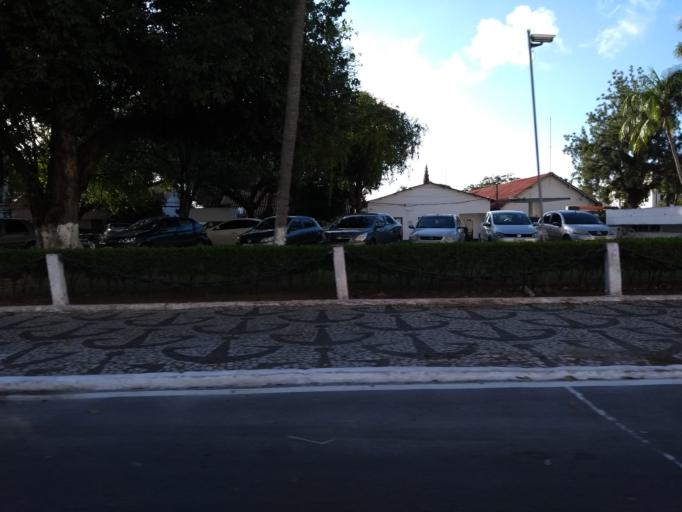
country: BR
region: Bahia
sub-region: Salvador
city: Salvador
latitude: -12.9753
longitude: -38.5150
